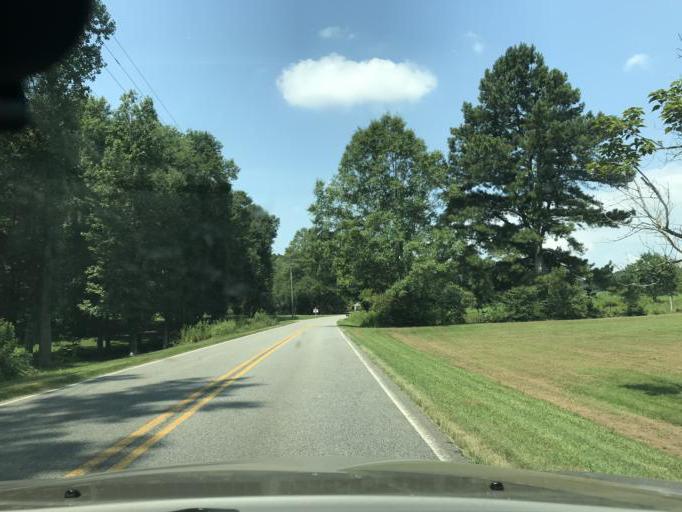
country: US
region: Georgia
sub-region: Forsyth County
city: Cumming
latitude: 34.2955
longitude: -84.1052
